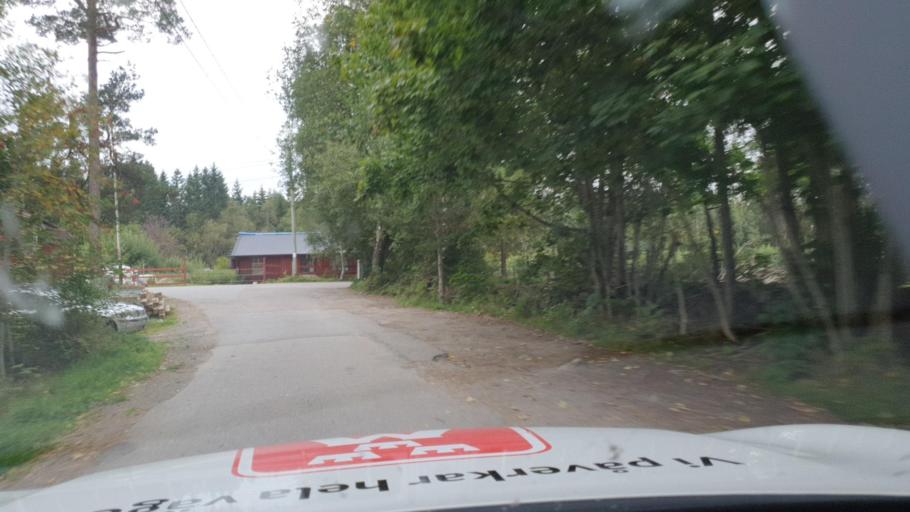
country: SE
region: Vaestra Goetaland
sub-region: Harryda Kommun
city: Hindas
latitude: 57.6994
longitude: 12.4647
